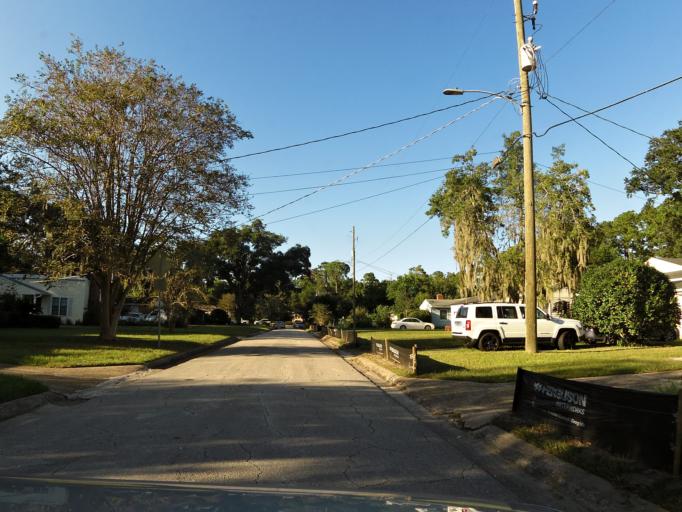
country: US
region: Florida
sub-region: Duval County
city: Jacksonville
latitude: 30.2672
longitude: -81.6401
